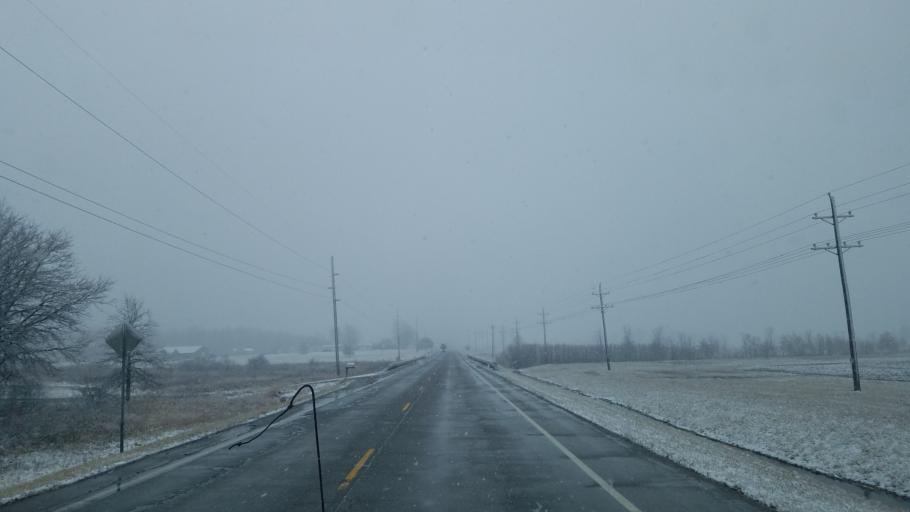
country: US
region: Ohio
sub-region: Champaign County
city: North Lewisburg
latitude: 40.3278
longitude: -83.5288
